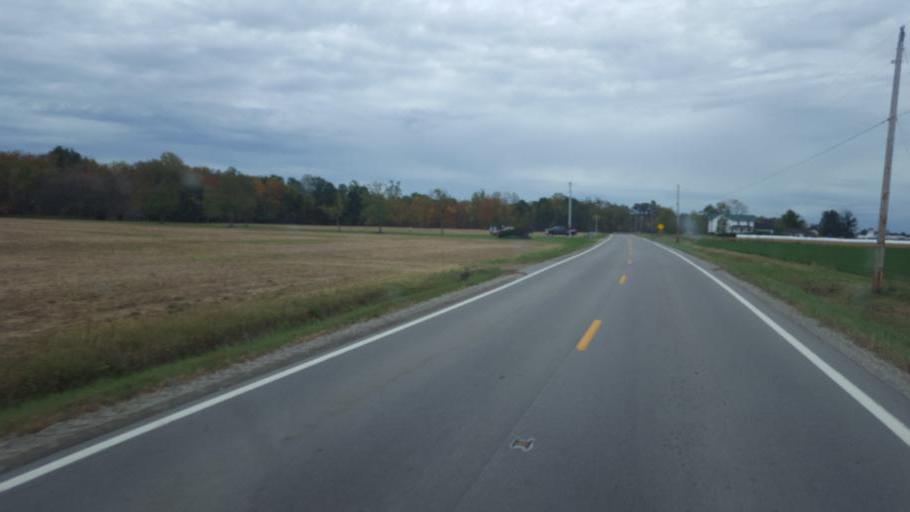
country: US
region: Ohio
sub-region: Huron County
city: Wakeman
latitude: 41.2378
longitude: -82.3943
